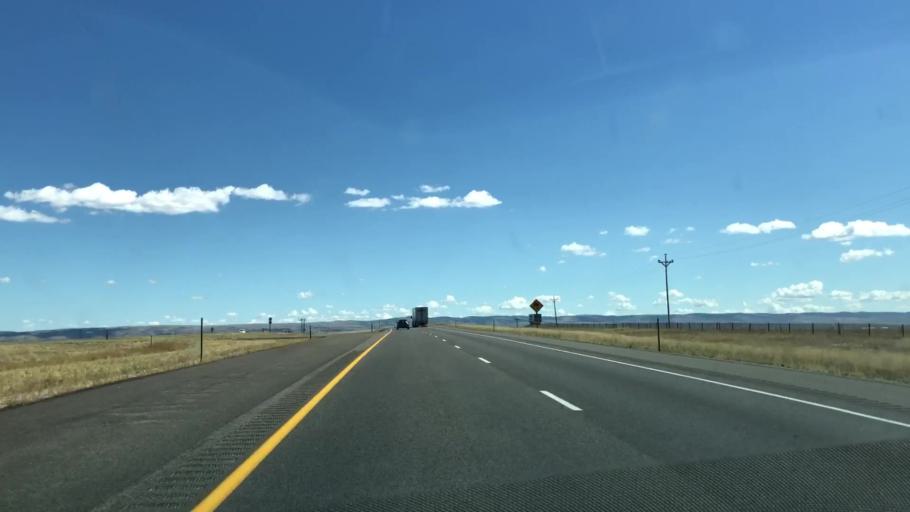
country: US
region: Wyoming
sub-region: Albany County
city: Laramie
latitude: 41.3496
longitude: -105.7089
